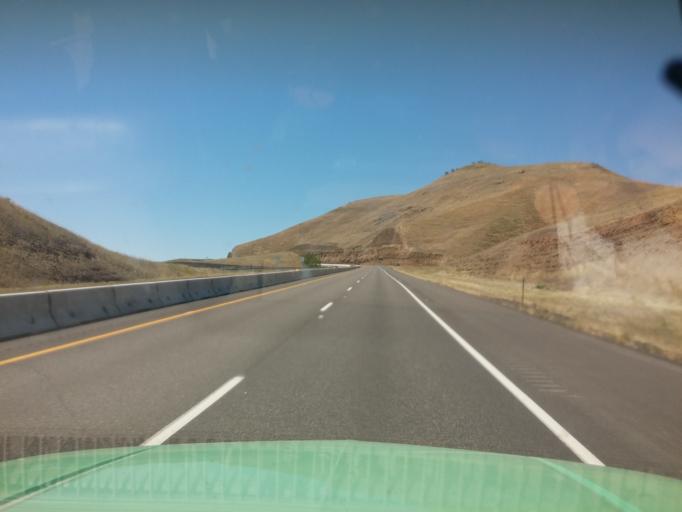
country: US
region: Idaho
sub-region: Nez Perce County
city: Lewiston
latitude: 46.4611
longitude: -116.9623
